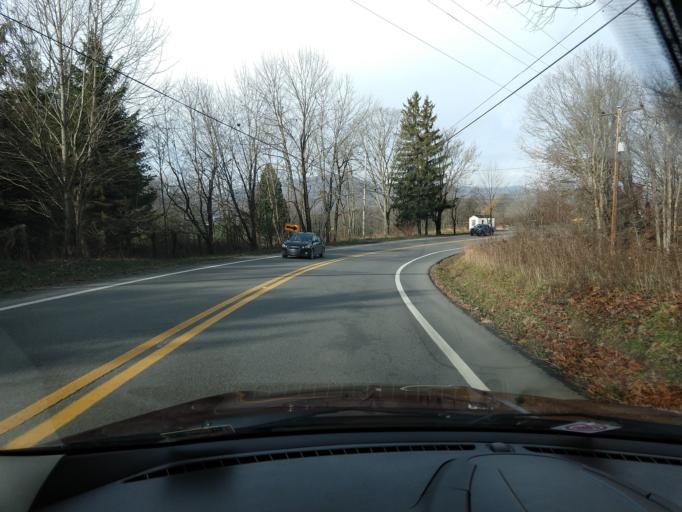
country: US
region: West Virginia
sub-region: Greenbrier County
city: Rainelle
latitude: 37.9297
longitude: -80.6507
